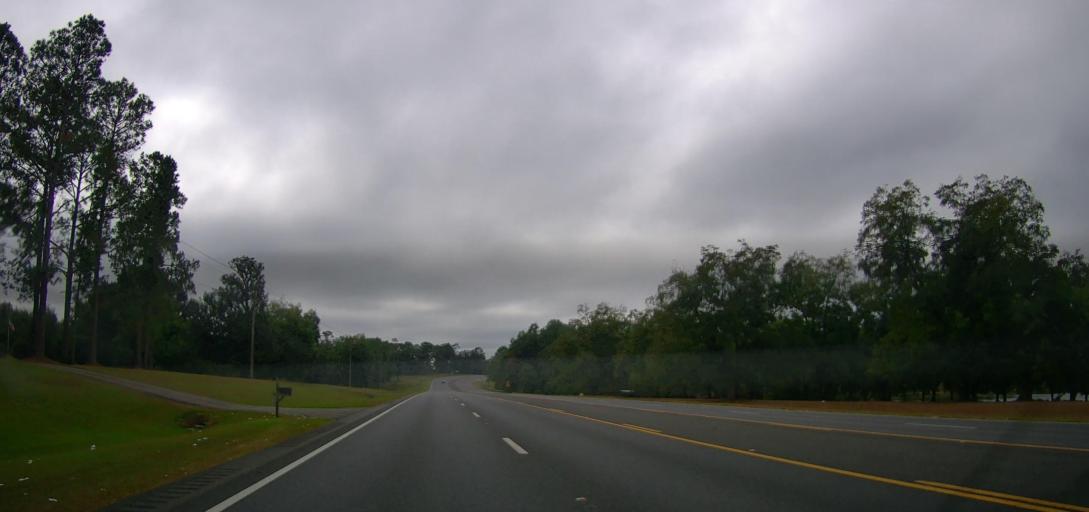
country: US
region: Georgia
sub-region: Thomas County
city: Thomasville
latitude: 30.9547
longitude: -83.8963
